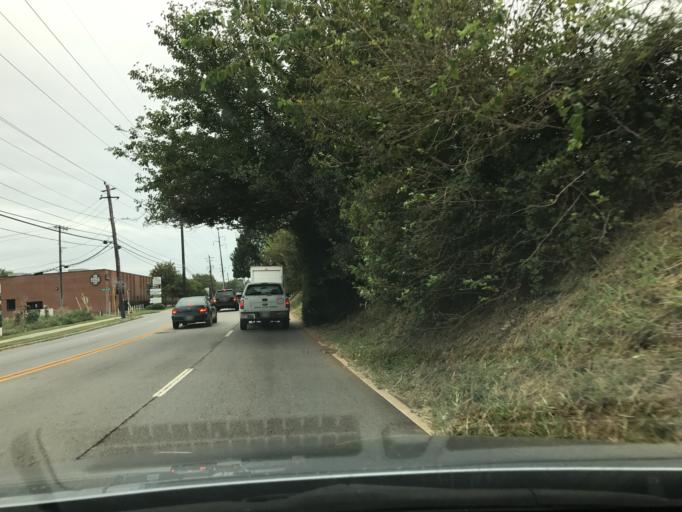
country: US
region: Georgia
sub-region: DeKalb County
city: Decatur
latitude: 33.7741
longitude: -84.2842
